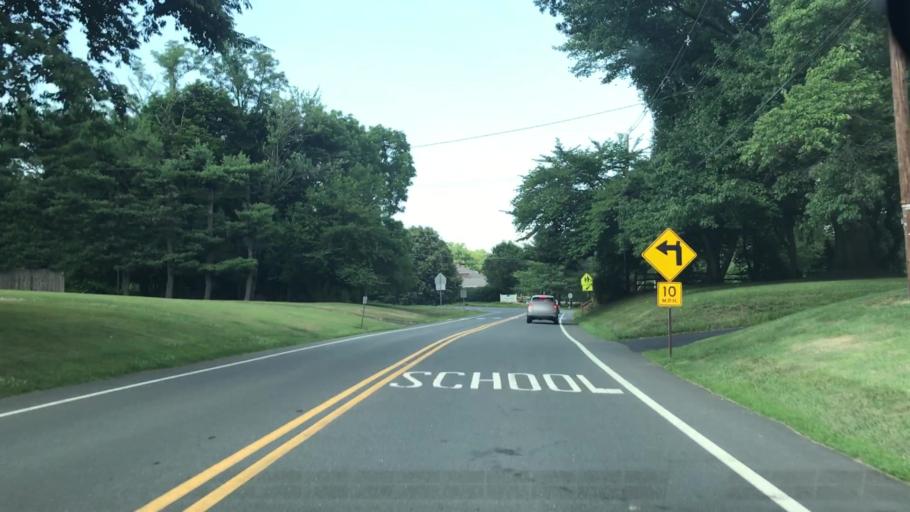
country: US
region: New Jersey
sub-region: Hunterdon County
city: Flemington
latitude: 40.5238
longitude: -74.7974
